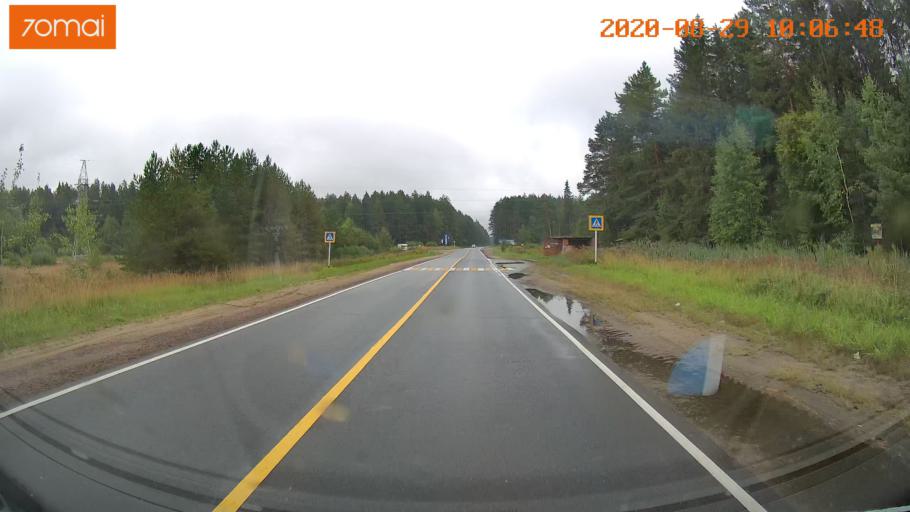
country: RU
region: Ivanovo
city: Kuznechikha
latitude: 57.3863
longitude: 42.5537
